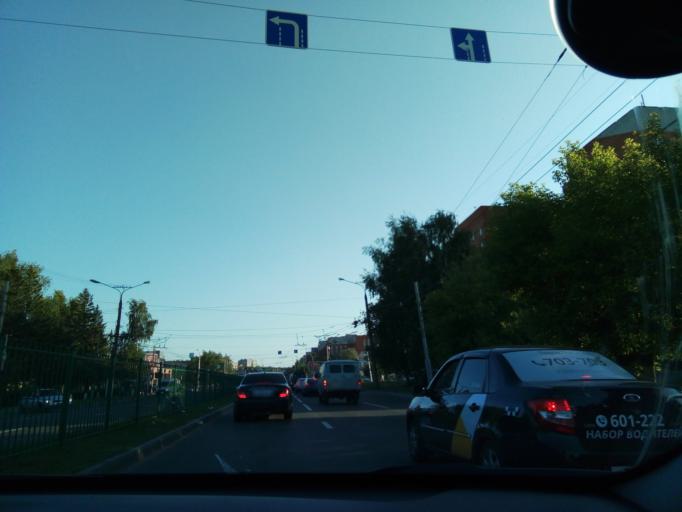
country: RU
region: Chuvashia
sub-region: Cheboksarskiy Rayon
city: Cheboksary
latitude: 56.1136
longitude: 47.2713
